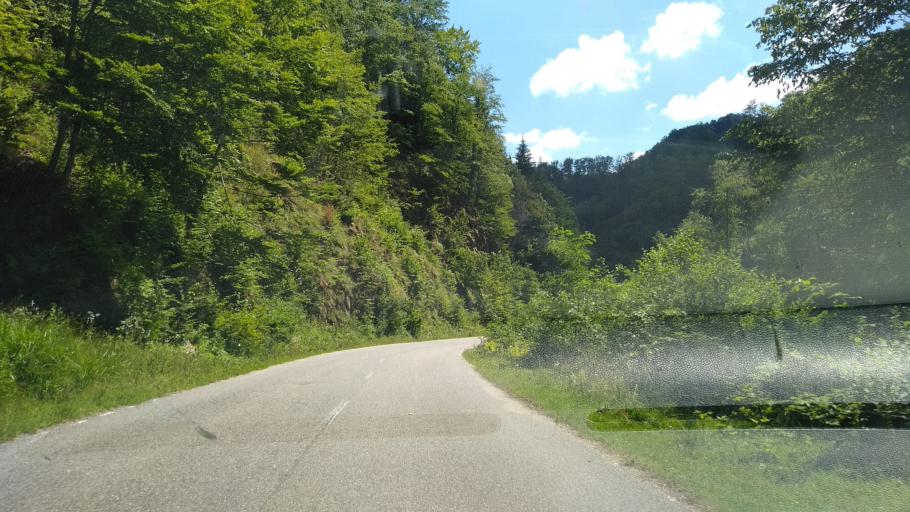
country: RO
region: Hunedoara
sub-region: Comuna Orastioara de Sus
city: Orastioara de Sus
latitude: 45.6356
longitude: 23.2016
